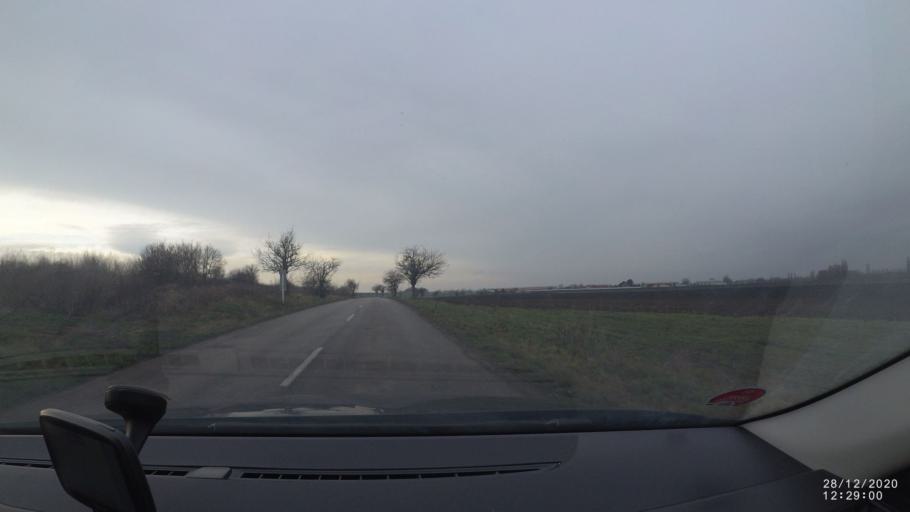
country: CZ
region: Central Bohemia
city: Brandys nad Labem-Stara Boleslav
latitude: 50.1964
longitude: 14.6233
